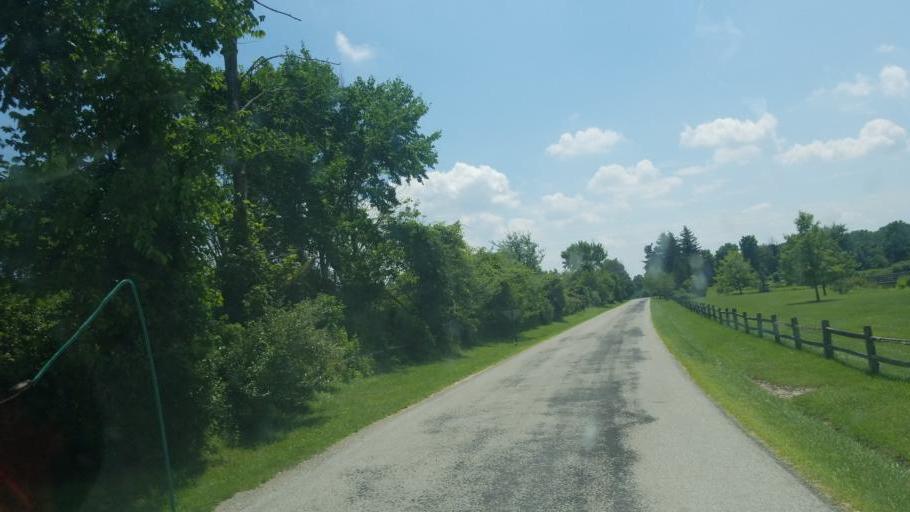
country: US
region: Ohio
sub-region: Richland County
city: Ontario
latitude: 40.8236
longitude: -82.5893
